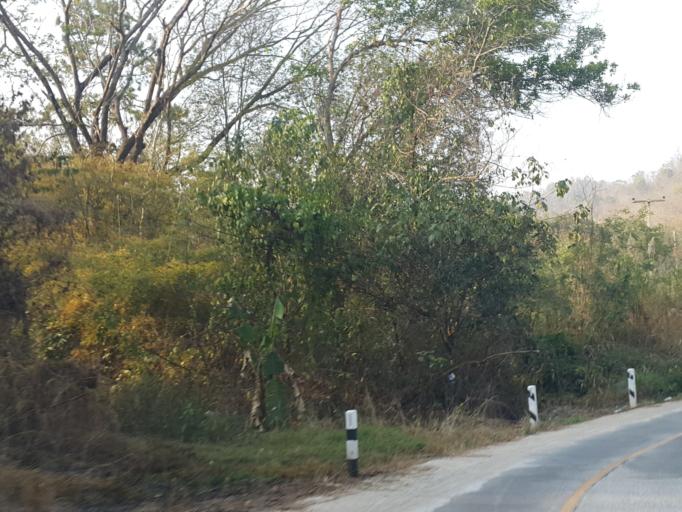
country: TH
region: Chiang Mai
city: Hang Dong
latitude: 18.7555
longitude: 98.8682
